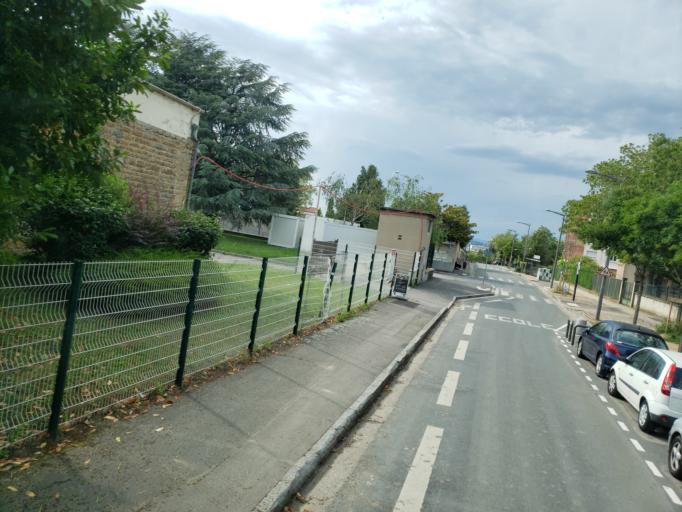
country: FR
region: Rhone-Alpes
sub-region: Departement du Rhone
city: Tassin-la-Demi-Lune
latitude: 45.7608
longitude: 4.8154
